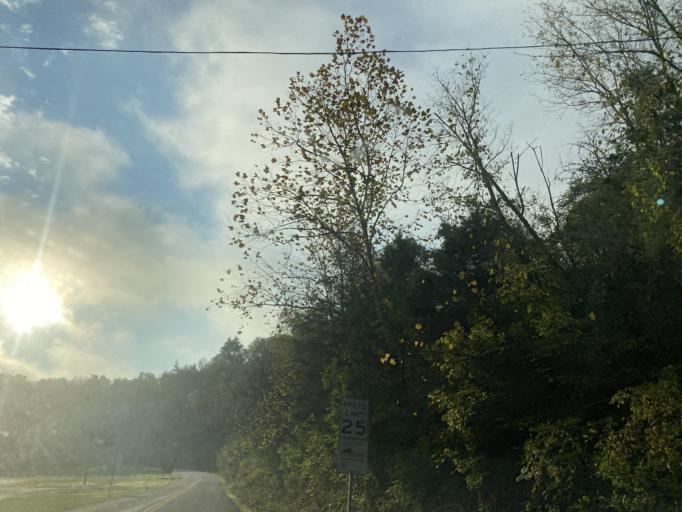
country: US
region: Kentucky
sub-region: Pendleton County
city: Falmouth
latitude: 38.7196
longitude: -84.3003
